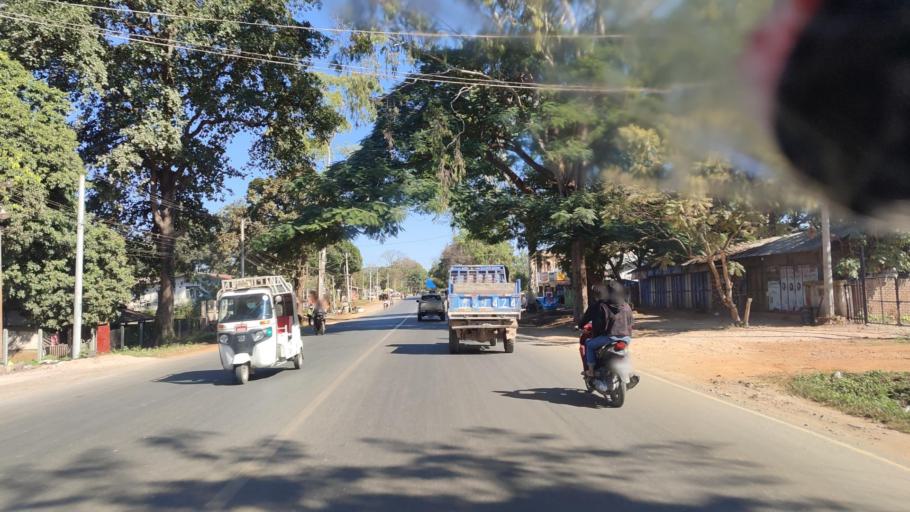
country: MM
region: Mandalay
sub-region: Pyin Oo Lwin District
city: Pyin Oo Lwin
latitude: 21.9798
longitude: 96.4102
